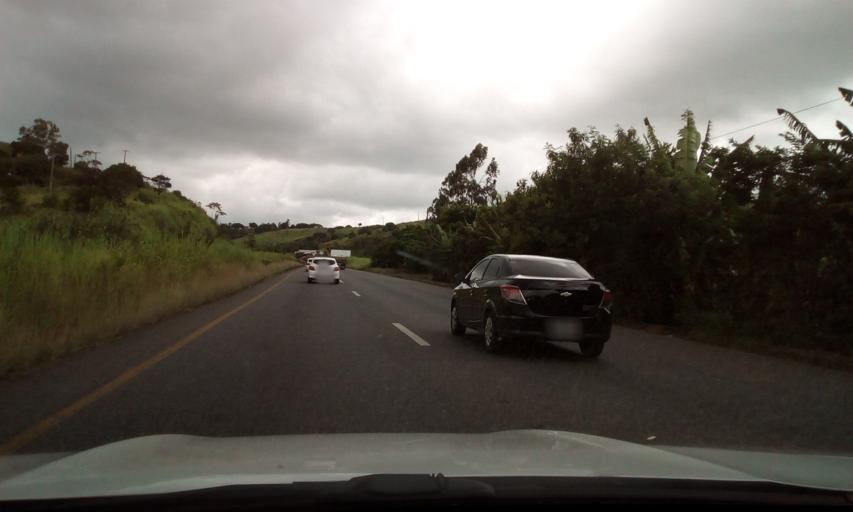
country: BR
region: Pernambuco
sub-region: Moreno
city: Moreno
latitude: -8.1107
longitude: -35.1514
